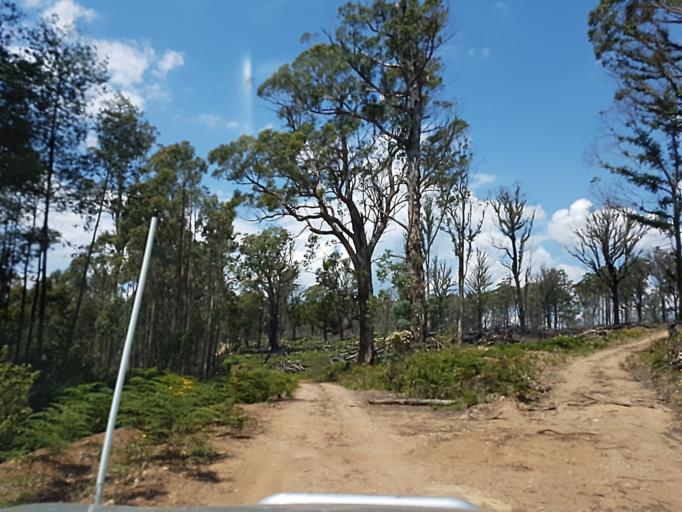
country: AU
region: Victoria
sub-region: East Gippsland
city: Lakes Entrance
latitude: -37.3865
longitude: 148.2834
